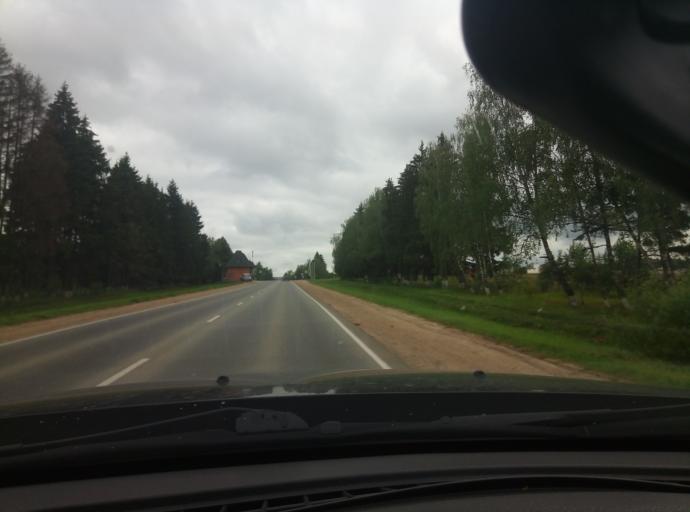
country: RU
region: Kaluga
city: Belousovo
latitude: 55.0732
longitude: 36.6875
